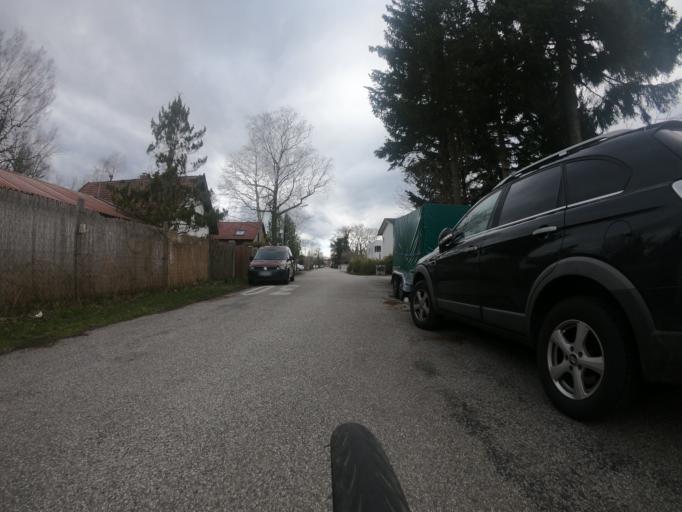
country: DE
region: Bavaria
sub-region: Upper Bavaria
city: Schongeising
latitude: 48.1581
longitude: 11.2267
